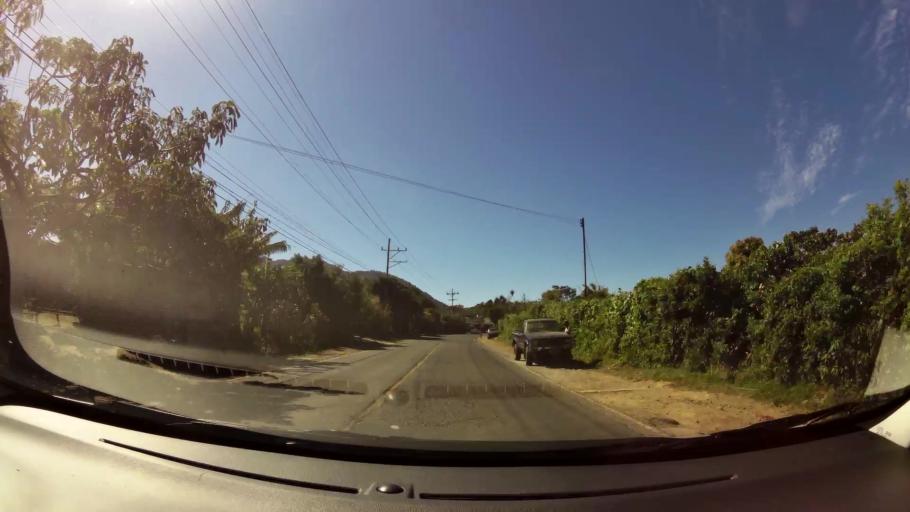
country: SV
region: Ahuachapan
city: Concepcion de Ataco
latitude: 13.8611
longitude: -89.8054
